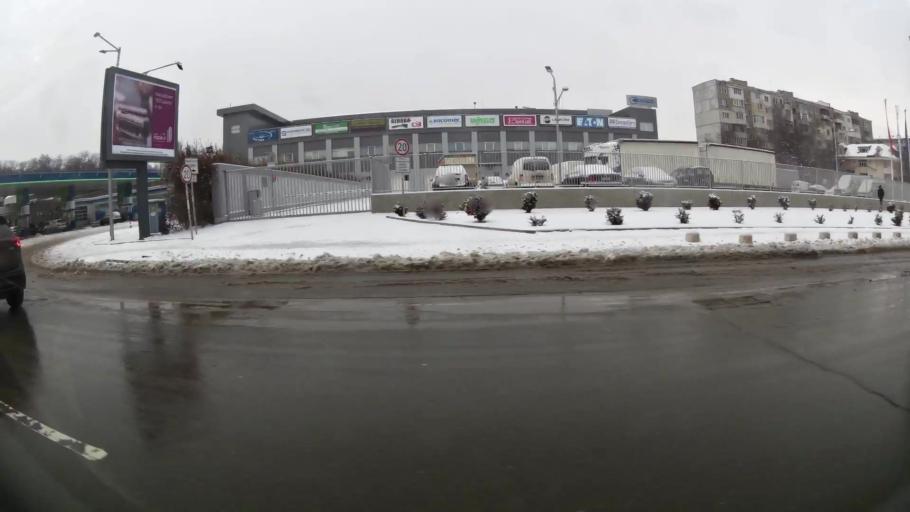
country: BG
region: Sofia-Capital
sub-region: Stolichna Obshtina
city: Sofia
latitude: 42.6916
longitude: 23.2956
